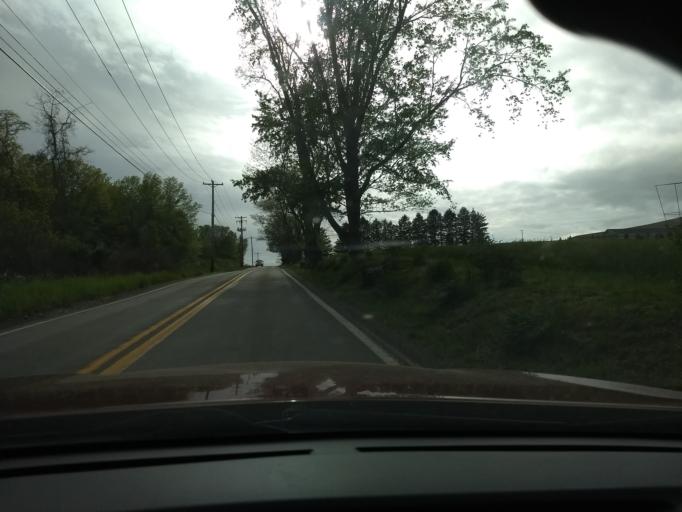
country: US
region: Pennsylvania
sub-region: Allegheny County
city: Russellton
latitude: 40.6005
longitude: -79.8908
